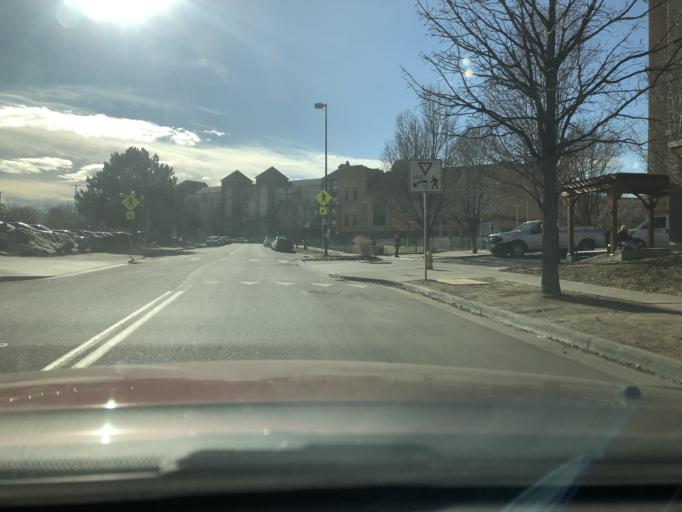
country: US
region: Colorado
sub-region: Denver County
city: Denver
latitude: 39.7489
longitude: -104.9781
